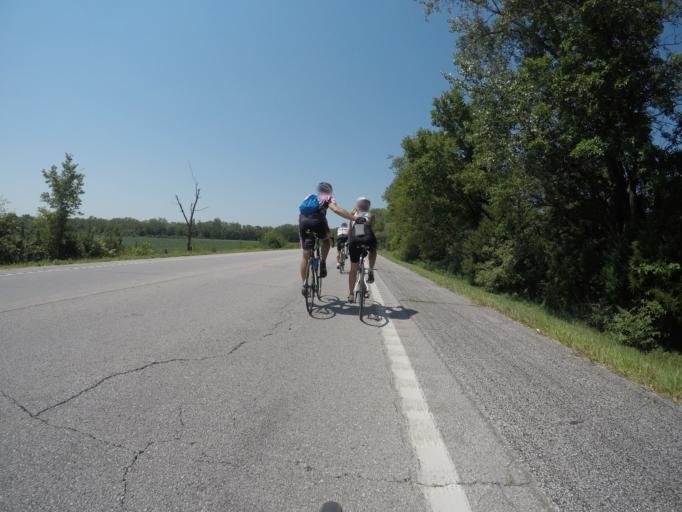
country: US
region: Kansas
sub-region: Leavenworth County
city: Leavenworth
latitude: 39.3293
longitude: -94.8859
